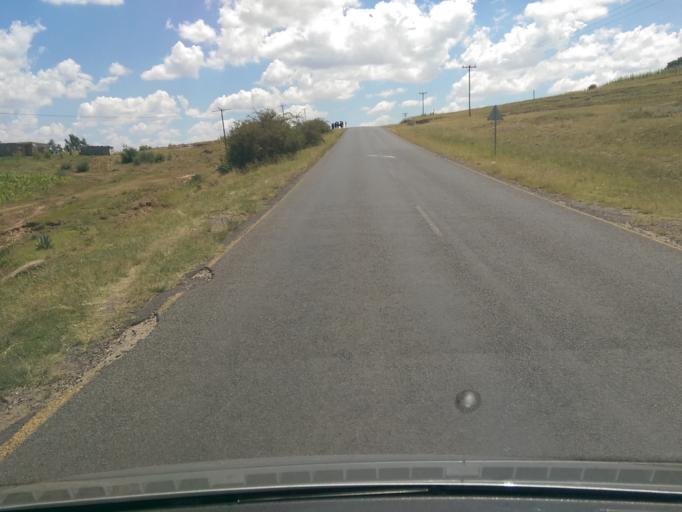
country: LS
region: Maseru
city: Nako
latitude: -29.4365
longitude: 27.6835
